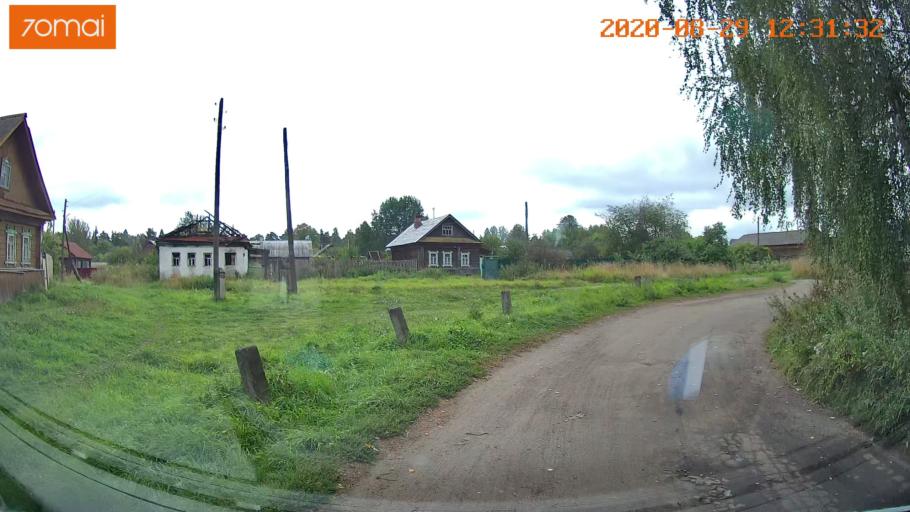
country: RU
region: Ivanovo
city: Yur'yevets
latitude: 57.3148
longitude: 43.1022
